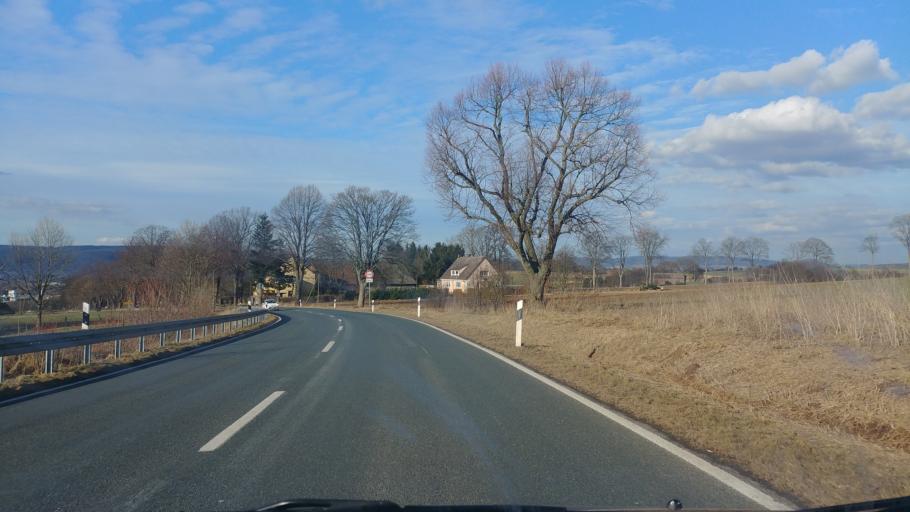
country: DE
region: Lower Saxony
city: Holzminden
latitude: 51.7962
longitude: 9.4503
